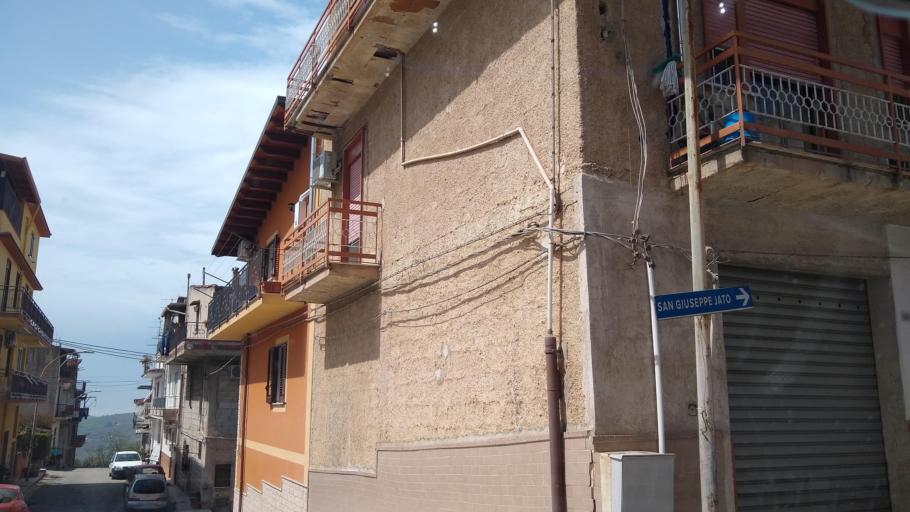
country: IT
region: Sicily
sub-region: Palermo
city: San Cipirello
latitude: 37.9645
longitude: 13.1760
